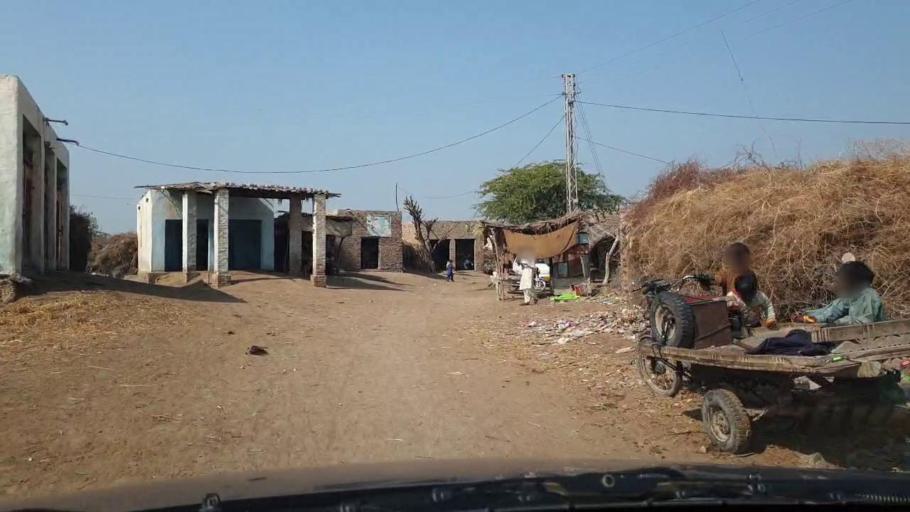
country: PK
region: Sindh
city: Jhol
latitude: 25.9047
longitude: 68.9976
